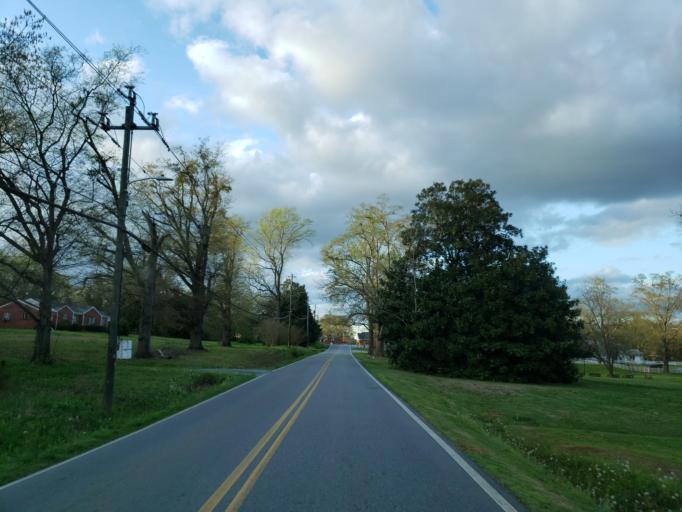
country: US
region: Georgia
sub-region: Polk County
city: Aragon
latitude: 34.0840
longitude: -84.9877
